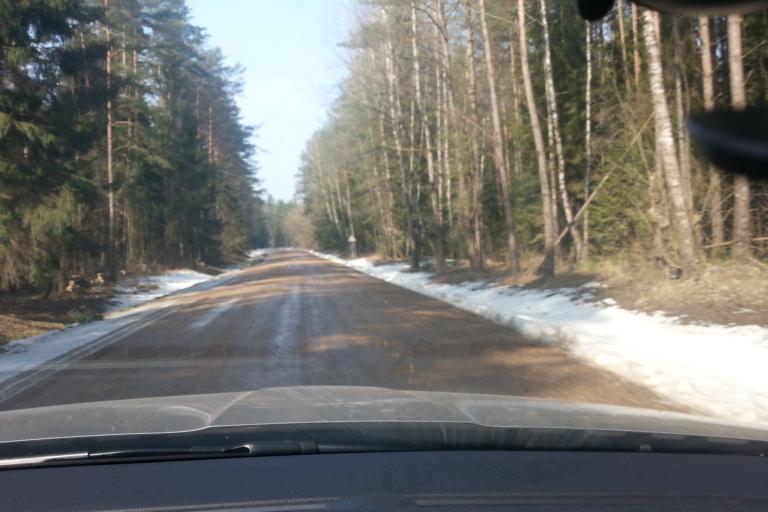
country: LT
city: Trakai
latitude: 54.5667
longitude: 24.9717
